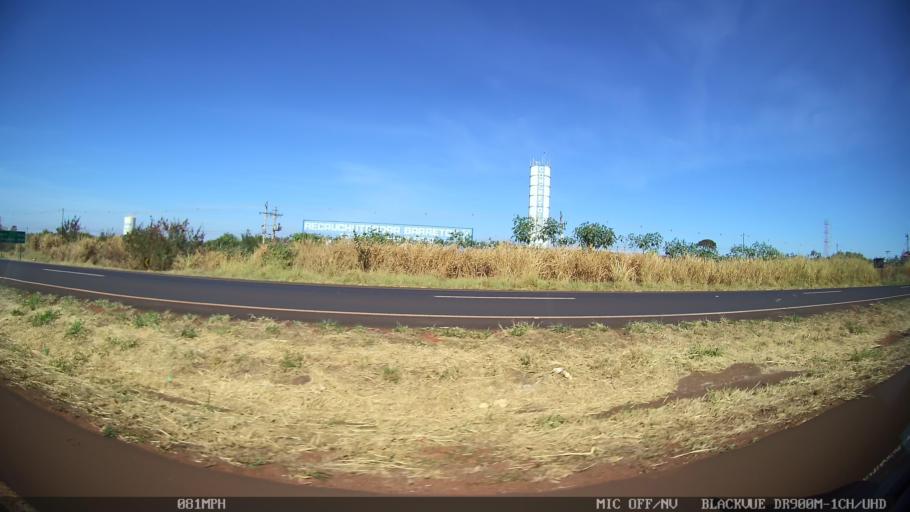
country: BR
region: Sao Paulo
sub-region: Barretos
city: Barretos
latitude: -20.5122
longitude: -48.5623
